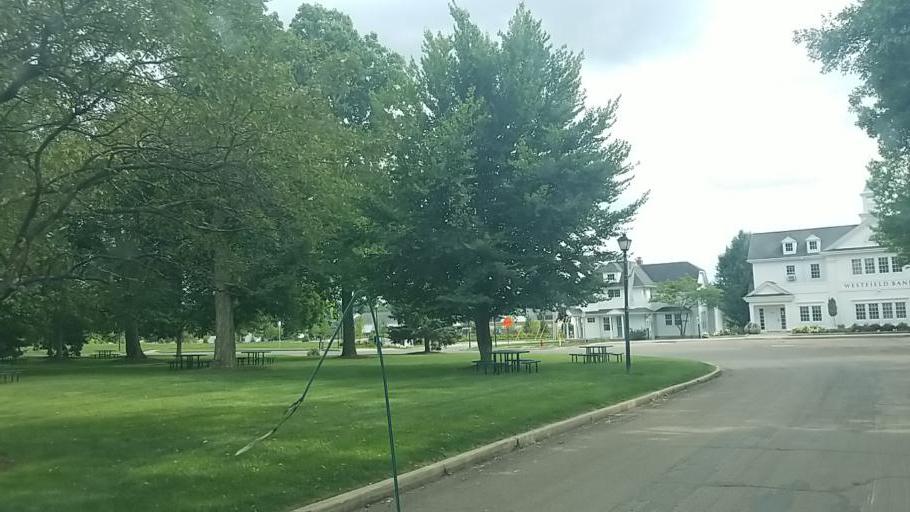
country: US
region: Ohio
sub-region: Medina County
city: Westfield Center
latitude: 41.0266
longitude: -81.9339
